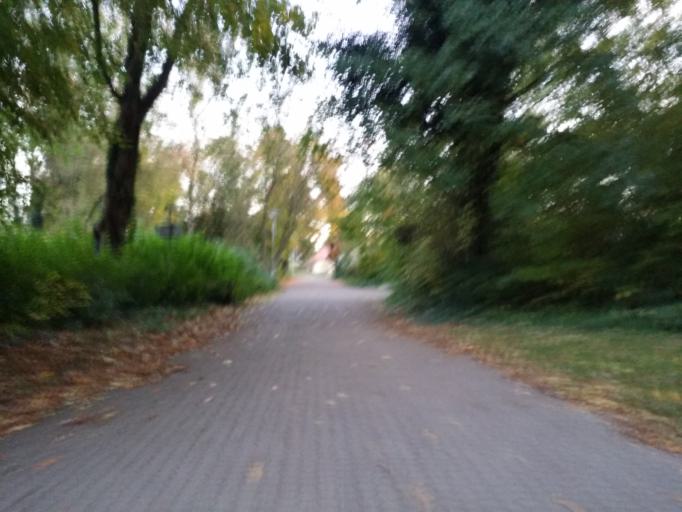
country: DE
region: Lower Saxony
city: Stuhr
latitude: 53.0417
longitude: 8.7429
